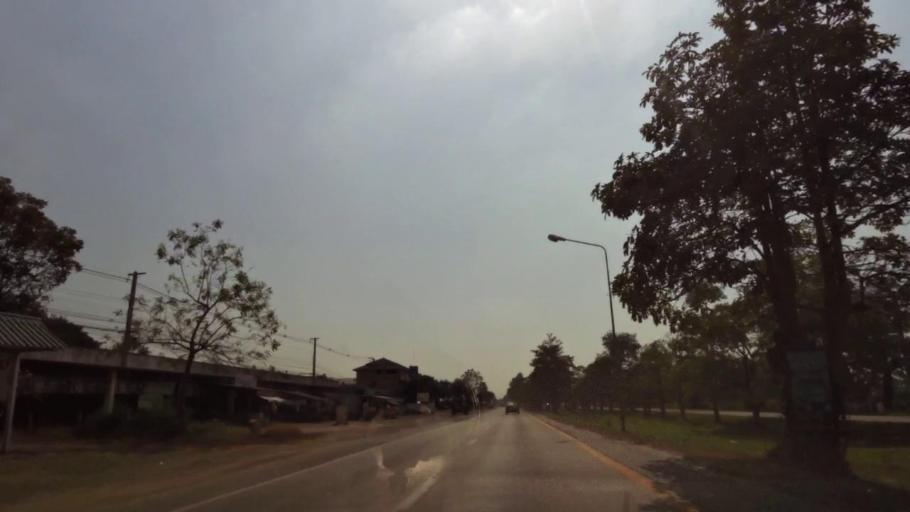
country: TH
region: Phichit
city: Wachira Barami
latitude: 16.5042
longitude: 100.1435
